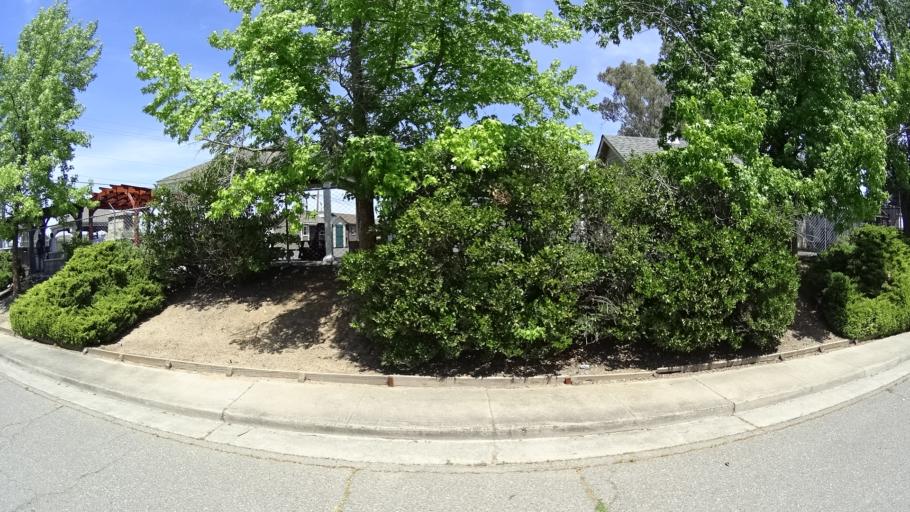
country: US
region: California
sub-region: Placer County
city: Rocklin
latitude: 38.7951
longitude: -121.2318
